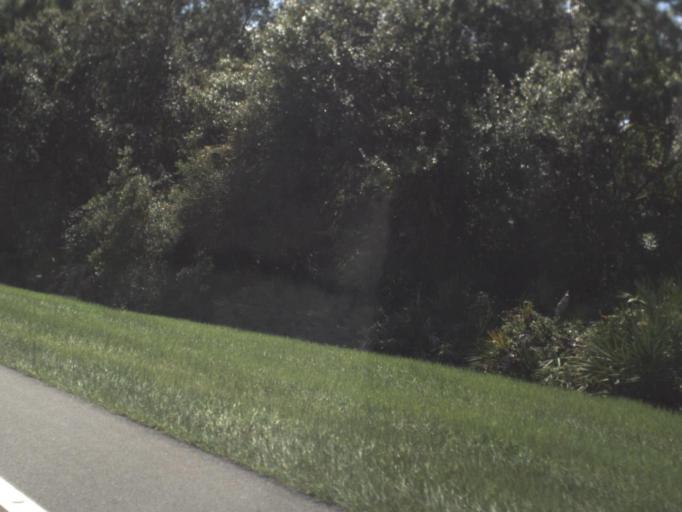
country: US
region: Florida
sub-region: Sarasota County
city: The Meadows
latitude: 27.4264
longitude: -82.3756
